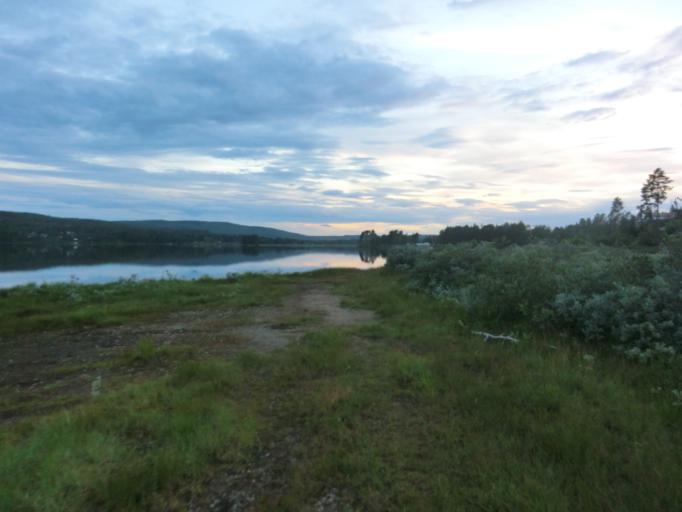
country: NO
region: Hedmark
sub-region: Trysil
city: Innbygda
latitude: 61.8533
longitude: 12.7440
